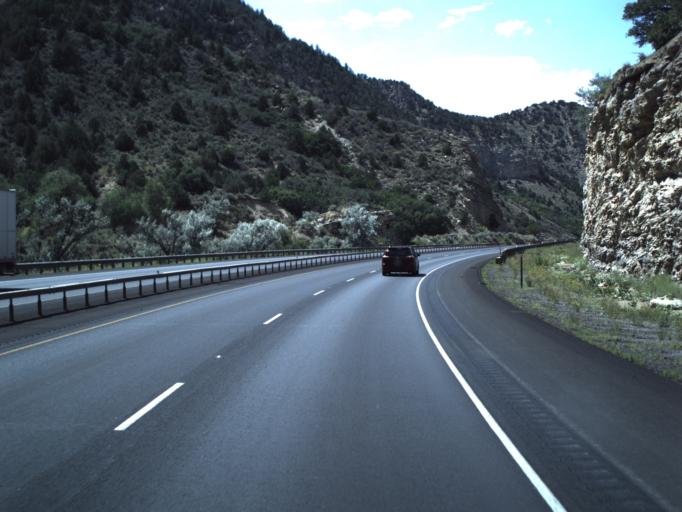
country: US
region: Utah
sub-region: Sevier County
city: Salina
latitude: 38.8981
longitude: -111.6466
